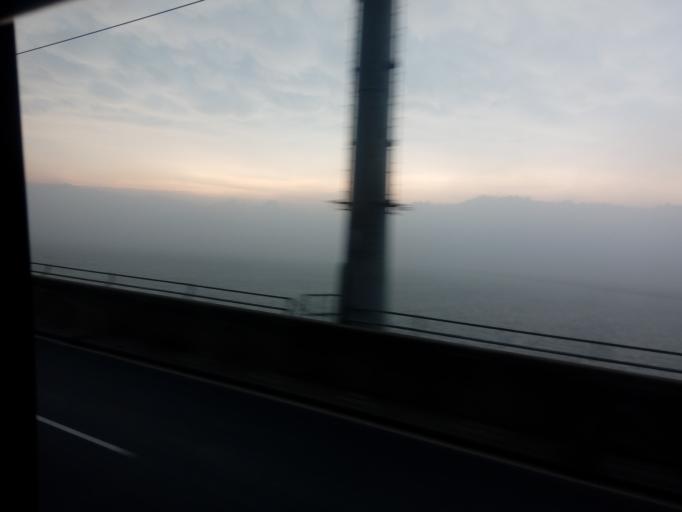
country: BD
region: Rajshahi
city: Sirajganj
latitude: 24.3996
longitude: 89.7796
